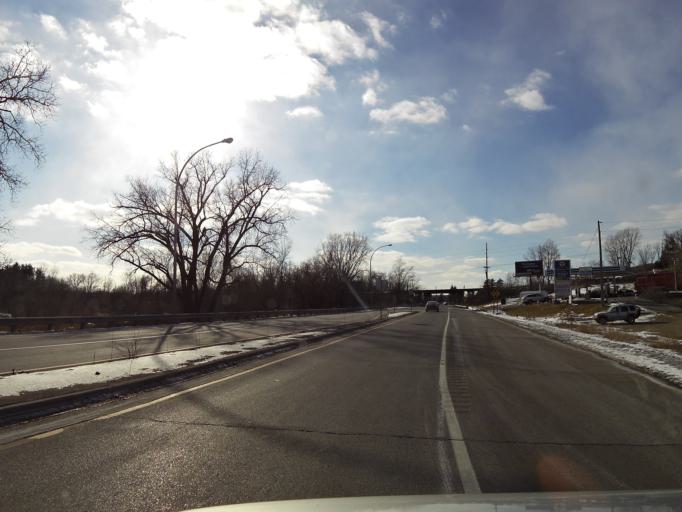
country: US
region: Minnesota
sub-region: Dakota County
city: Eagan
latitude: 44.8092
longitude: -93.1005
